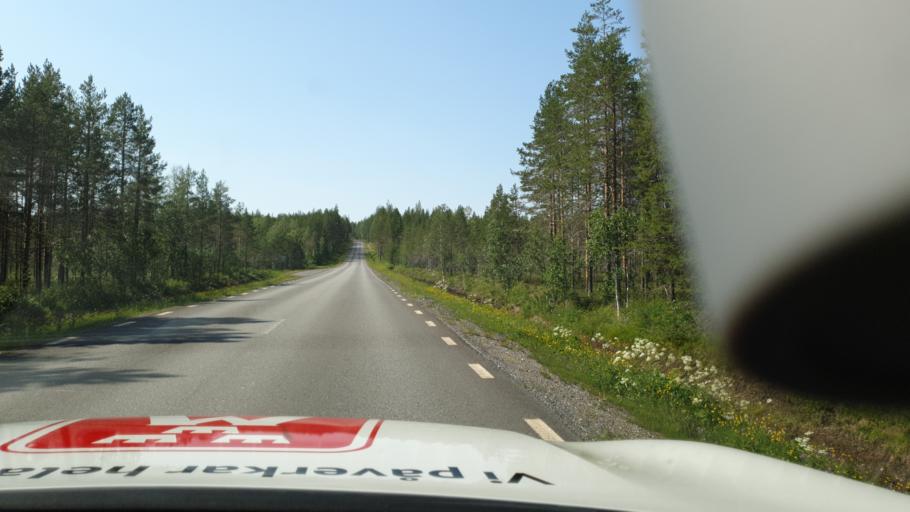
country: SE
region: Vaesterbotten
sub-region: Skelleftea Kommun
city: Langsele
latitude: 64.9796
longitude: 20.0623
